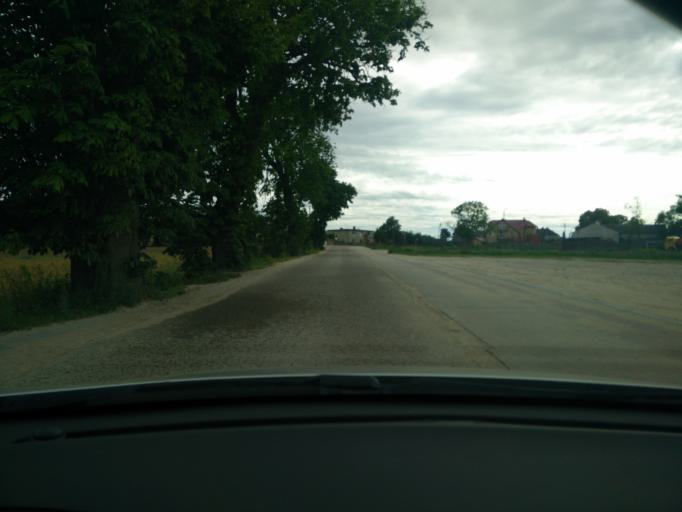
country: PL
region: Pomeranian Voivodeship
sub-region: Powiat pucki
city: Mrzezino
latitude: 54.6535
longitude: 18.4326
